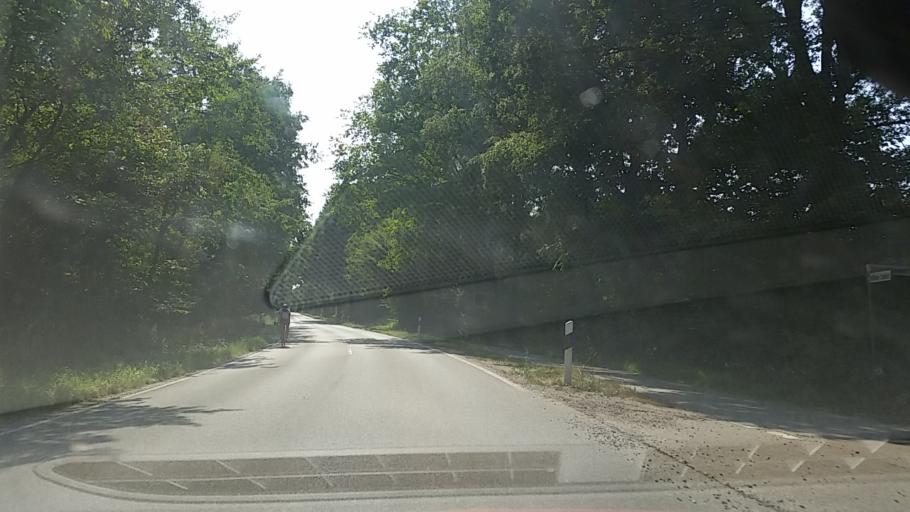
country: DE
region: Schleswig-Holstein
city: Witzhave
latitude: 53.5744
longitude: 10.3574
